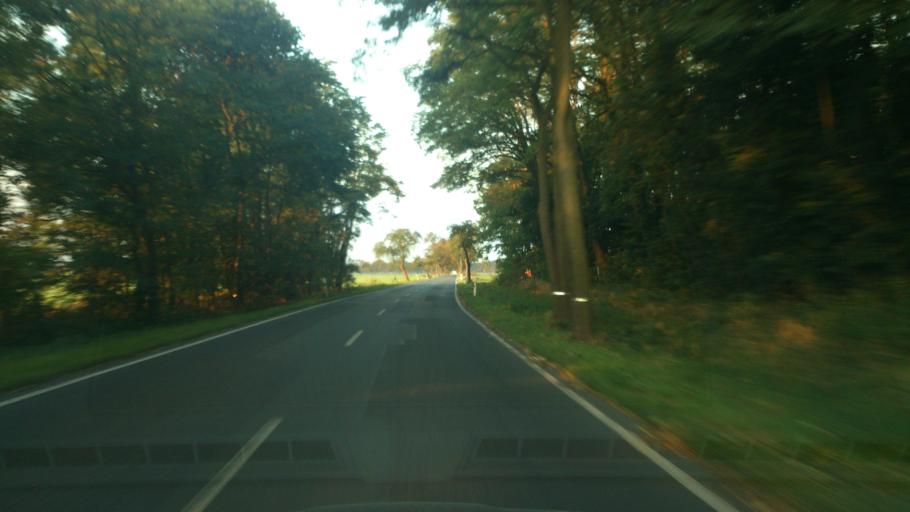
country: DE
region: Brandenburg
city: Rangsdorf
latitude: 52.2669
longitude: 13.3502
